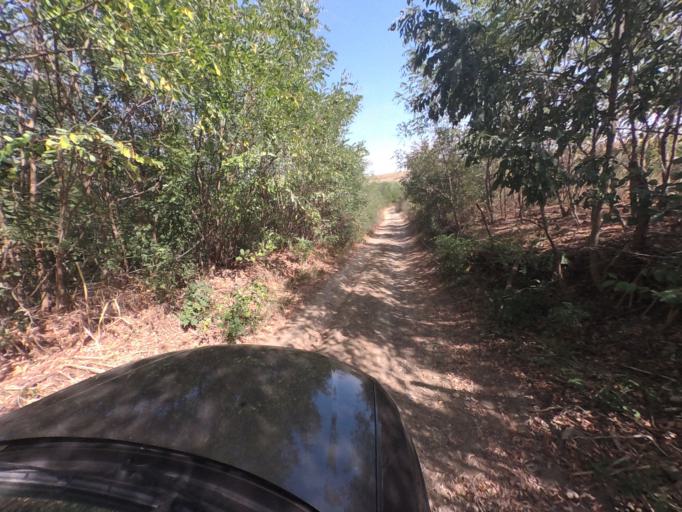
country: RO
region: Vaslui
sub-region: Comuna Costesti
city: Costesti
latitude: 46.5133
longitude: 27.7408
